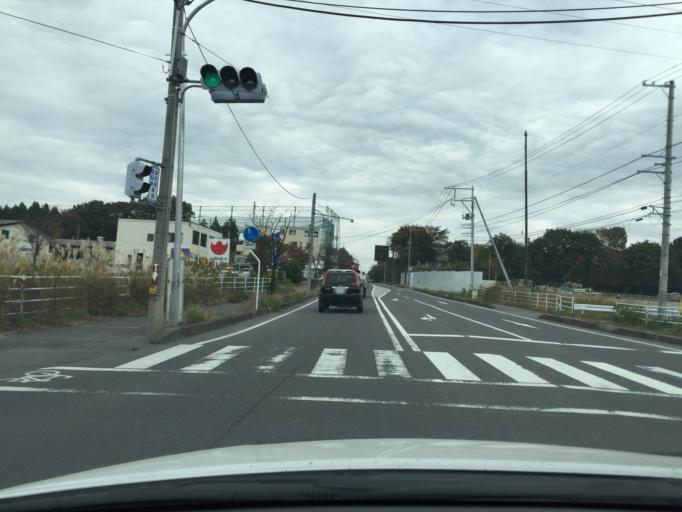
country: JP
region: Tochigi
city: Kuroiso
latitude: 37.1057
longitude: 140.2215
